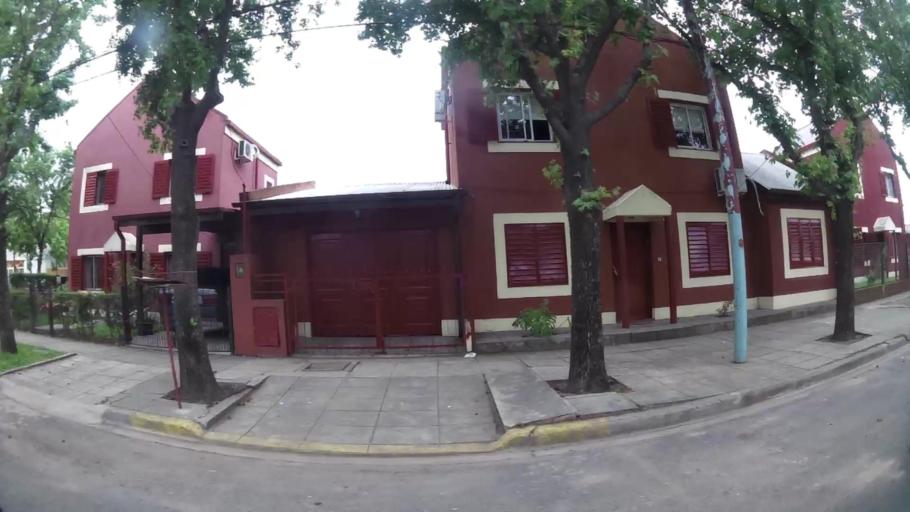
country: AR
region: Buenos Aires
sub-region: Partido de Campana
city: Campana
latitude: -34.1948
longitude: -58.9427
